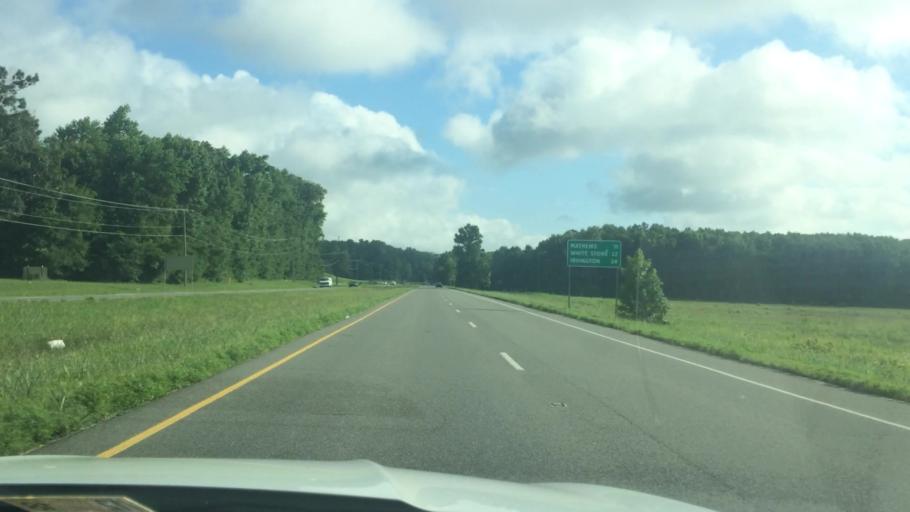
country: US
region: Virginia
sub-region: Gloucester County
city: Gloucester Courthouse
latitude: 37.4426
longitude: -76.4748
